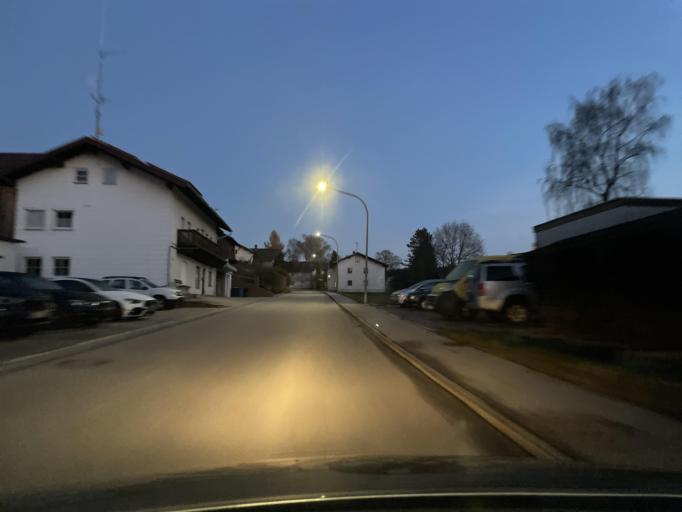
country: DE
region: Bavaria
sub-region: Lower Bavaria
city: Wittibreut
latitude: 48.3300
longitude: 12.9946
